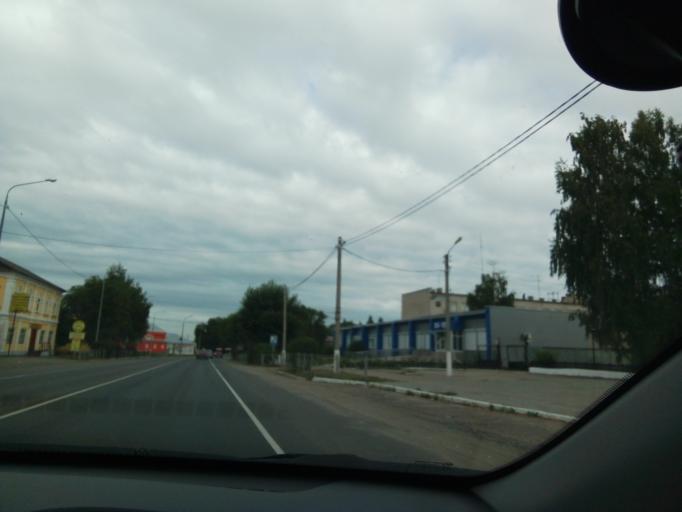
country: RU
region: Rjazan
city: Shatsk
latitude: 54.0254
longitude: 41.7101
